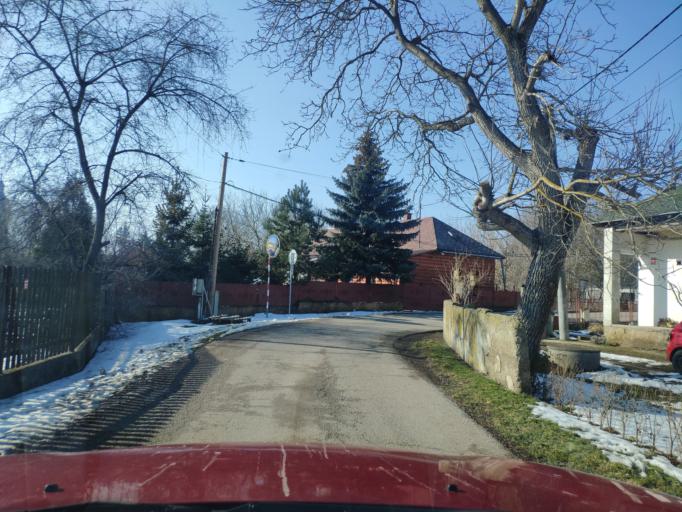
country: HU
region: Borsod-Abauj-Zemplen
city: Gonc
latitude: 48.5810
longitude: 21.2732
